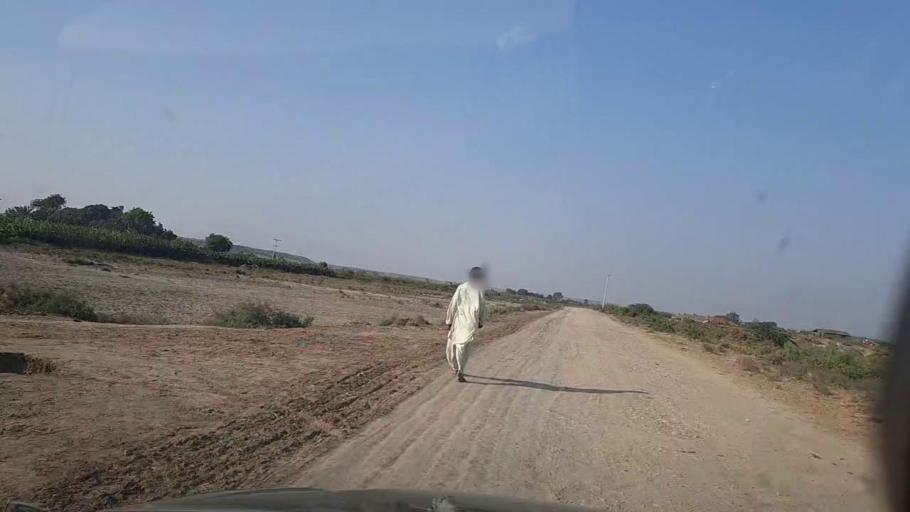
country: PK
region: Sindh
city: Thatta
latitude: 24.5969
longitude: 67.8746
